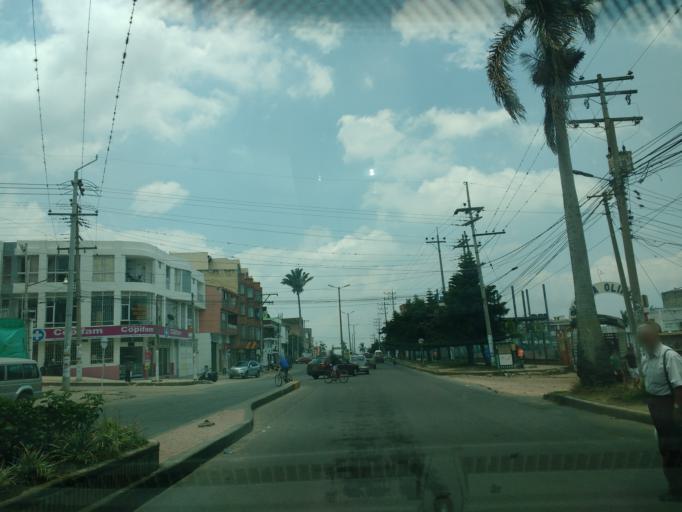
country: CO
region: Cundinamarca
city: Fusagasuga
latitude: 4.3354
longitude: -74.3673
